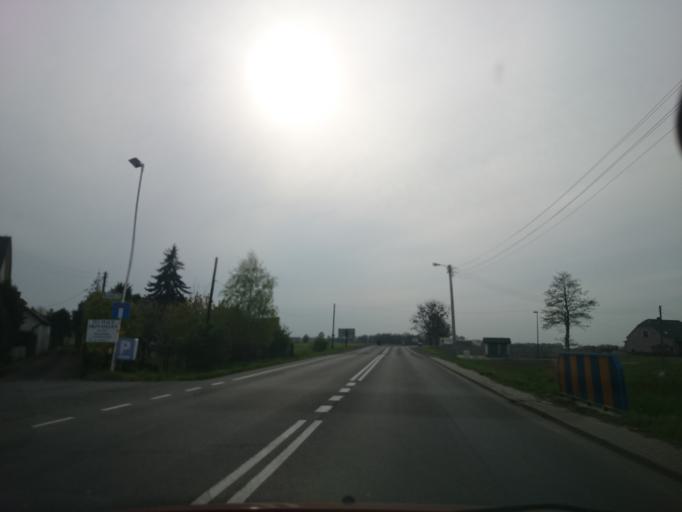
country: PL
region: Opole Voivodeship
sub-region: Powiat opolski
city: Chroscina
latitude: 50.6812
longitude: 17.8484
